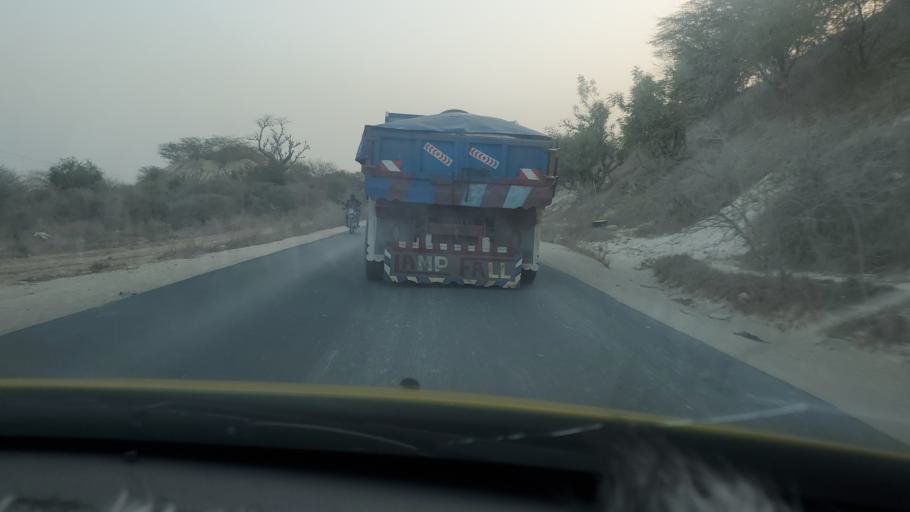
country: SN
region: Thies
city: Nguekhokh
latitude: 14.6352
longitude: -16.9935
